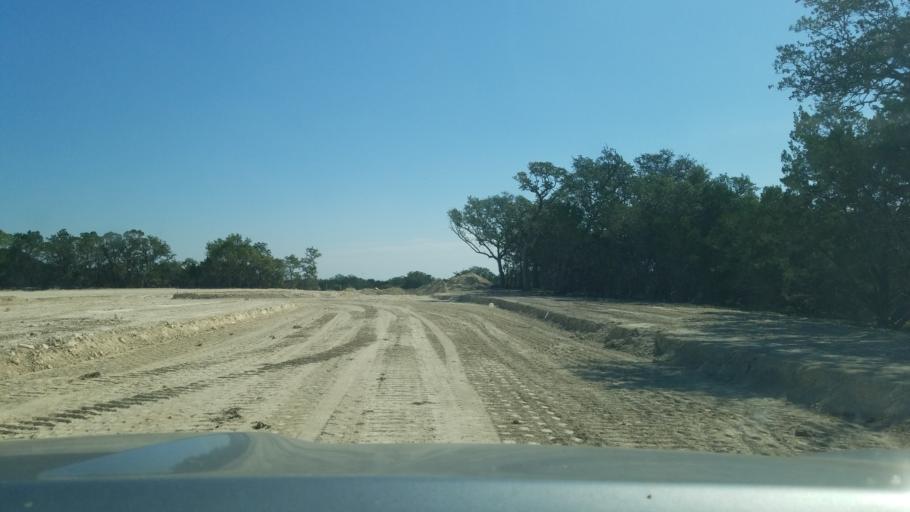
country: US
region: Texas
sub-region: Kendall County
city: Boerne
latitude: 29.7568
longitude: -98.7180
